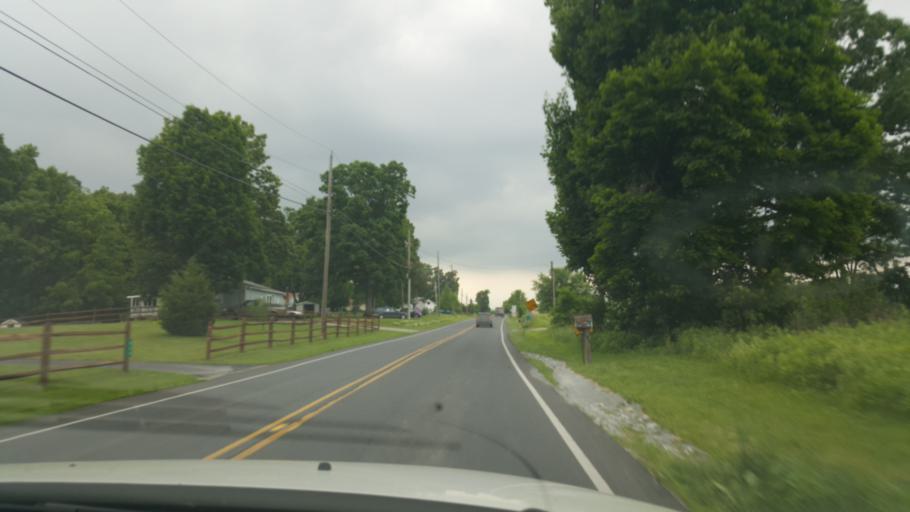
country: US
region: Pennsylvania
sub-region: Adams County
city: Lake Meade
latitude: 39.9486
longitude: -77.1024
